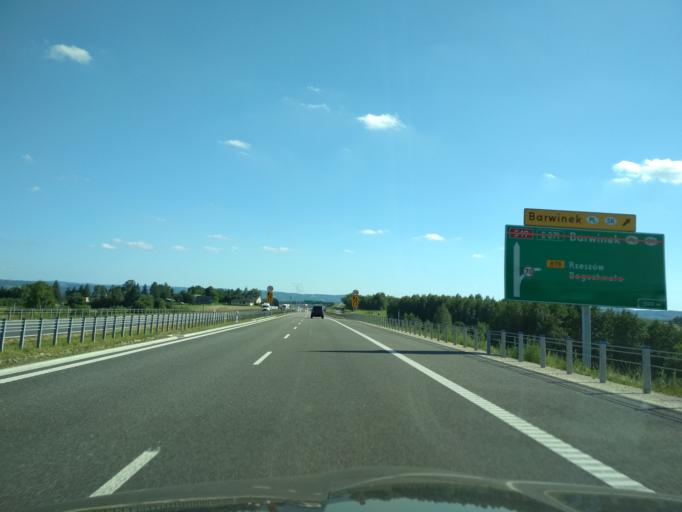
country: PL
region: Subcarpathian Voivodeship
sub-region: Powiat rzeszowski
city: Kielanowka
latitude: 50.0228
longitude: 21.9220
